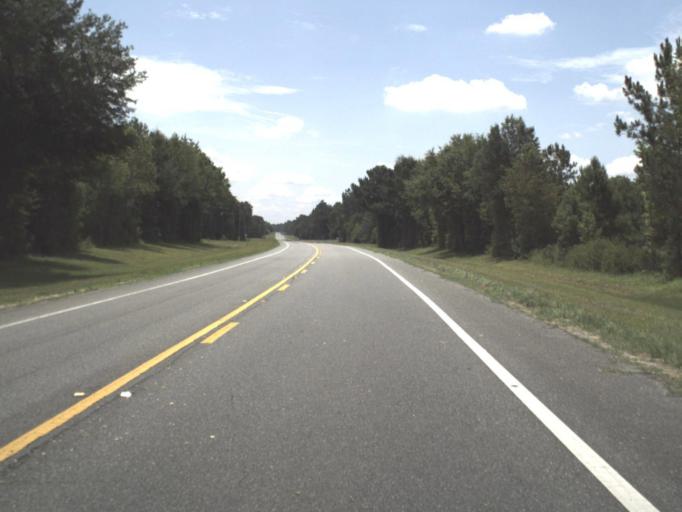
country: US
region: Florida
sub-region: Suwannee County
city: Live Oak
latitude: 30.1769
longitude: -82.9831
